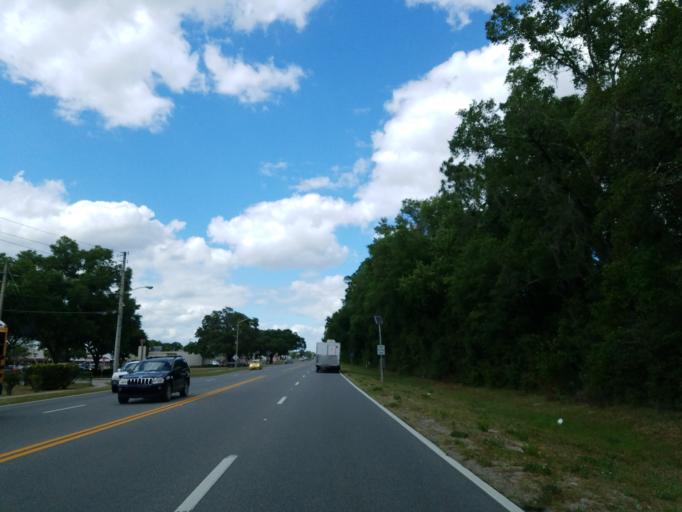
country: US
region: Florida
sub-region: Sumter County
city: Bushnell
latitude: 28.6736
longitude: -82.1118
